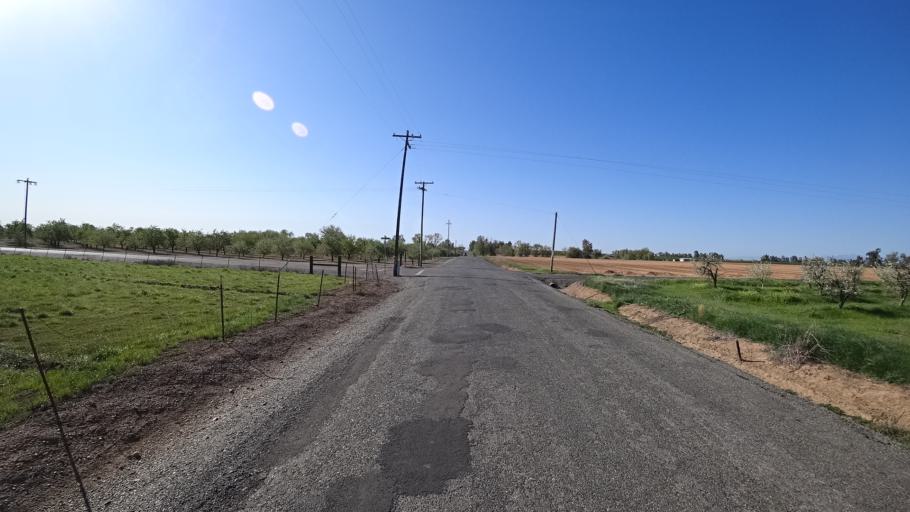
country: US
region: California
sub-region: Glenn County
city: Hamilton City
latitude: 39.7900
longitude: -122.0665
